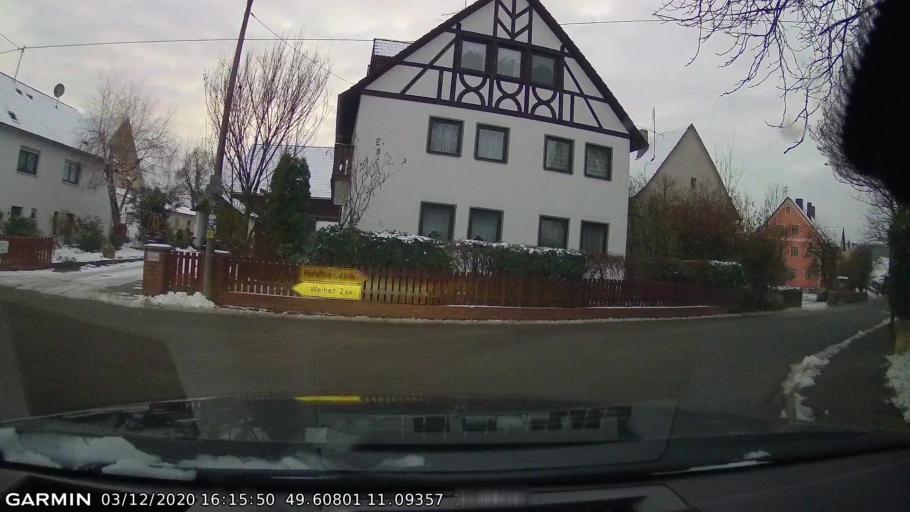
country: DE
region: Bavaria
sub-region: Regierungsbezirk Mittelfranken
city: Uttenreuth
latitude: 49.6081
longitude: 11.0937
